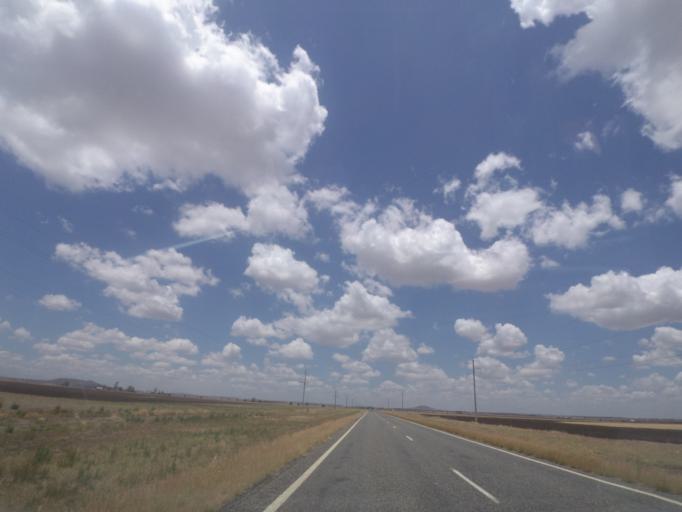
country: AU
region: Queensland
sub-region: Toowoomba
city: Top Camp
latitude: -27.8988
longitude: 151.9756
